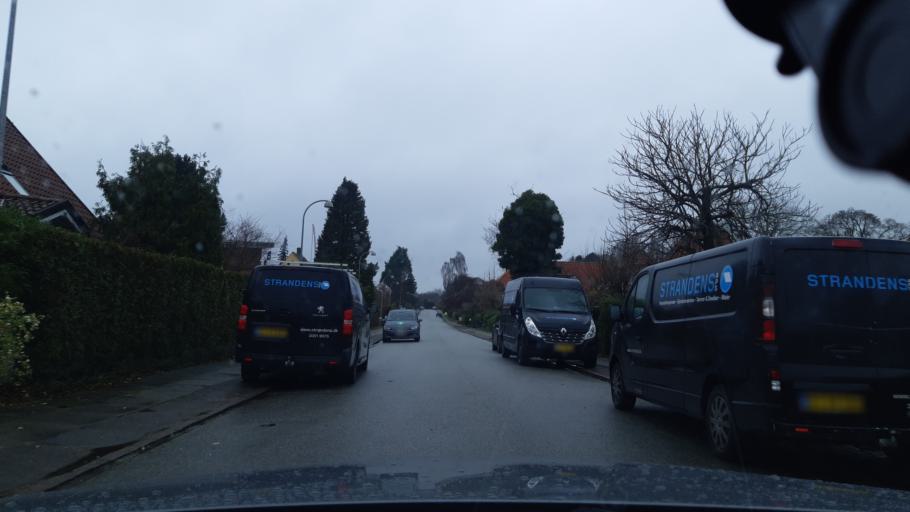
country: DK
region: Capital Region
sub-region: Herlev Kommune
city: Herlev
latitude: 55.7623
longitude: 12.4482
